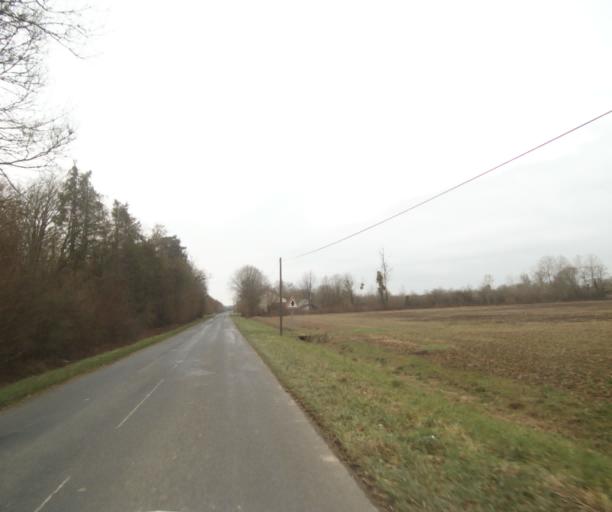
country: FR
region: Champagne-Ardenne
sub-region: Departement de la Haute-Marne
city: Villiers-en-Lieu
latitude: 48.6557
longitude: 4.8773
